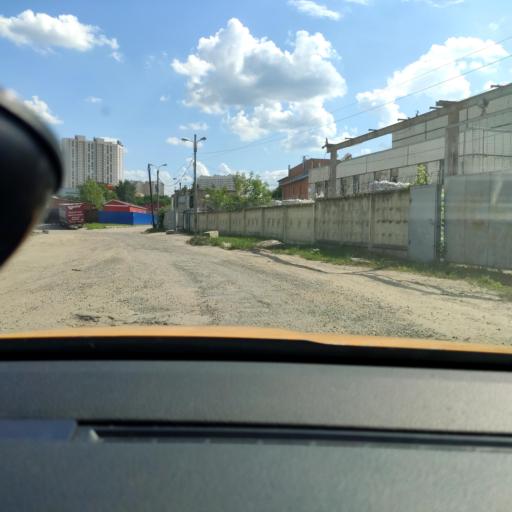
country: RU
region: Moskovskaya
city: Kotel'niki
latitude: 55.6446
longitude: 37.8455
